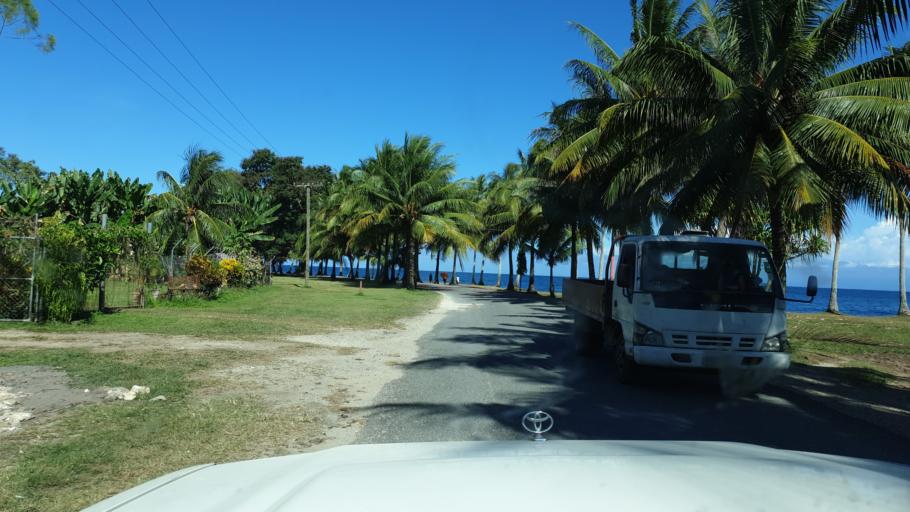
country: PG
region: Madang
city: Madang
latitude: -5.2273
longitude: 145.8021
